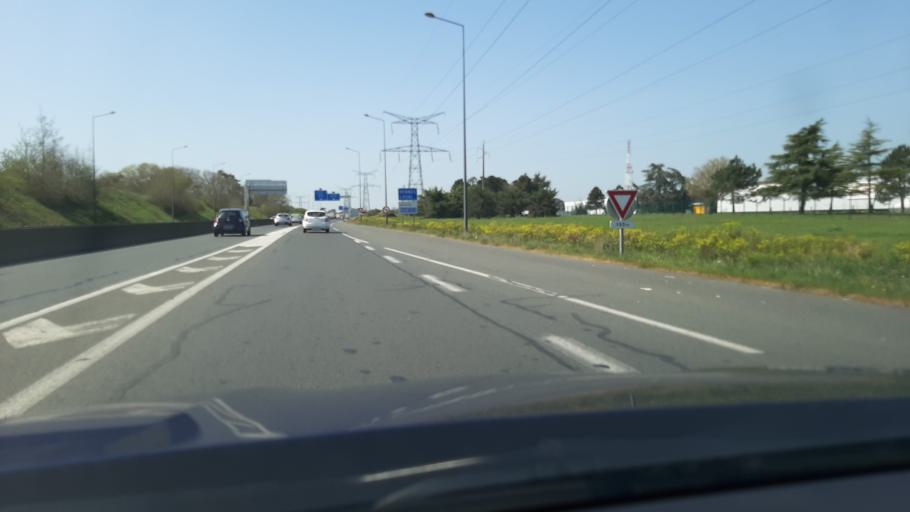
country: FR
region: Pays de la Loire
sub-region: Departement de Maine-et-Loire
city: Trelaze
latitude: 47.4723
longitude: -0.4975
